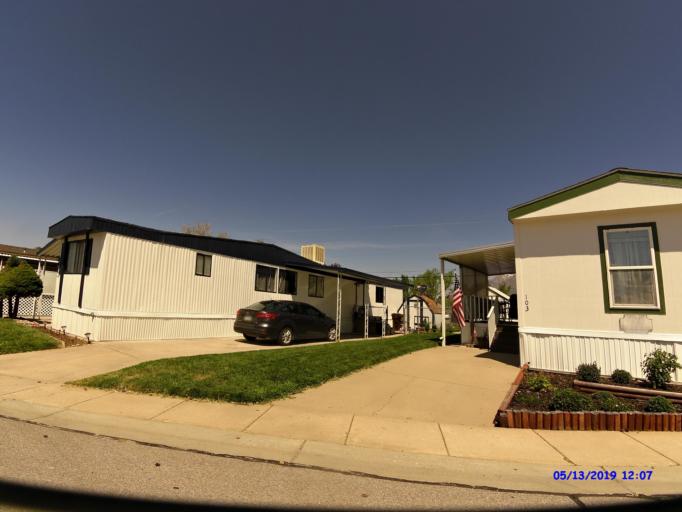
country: US
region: Utah
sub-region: Weber County
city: Harrisville
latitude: 41.2766
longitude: -111.9647
